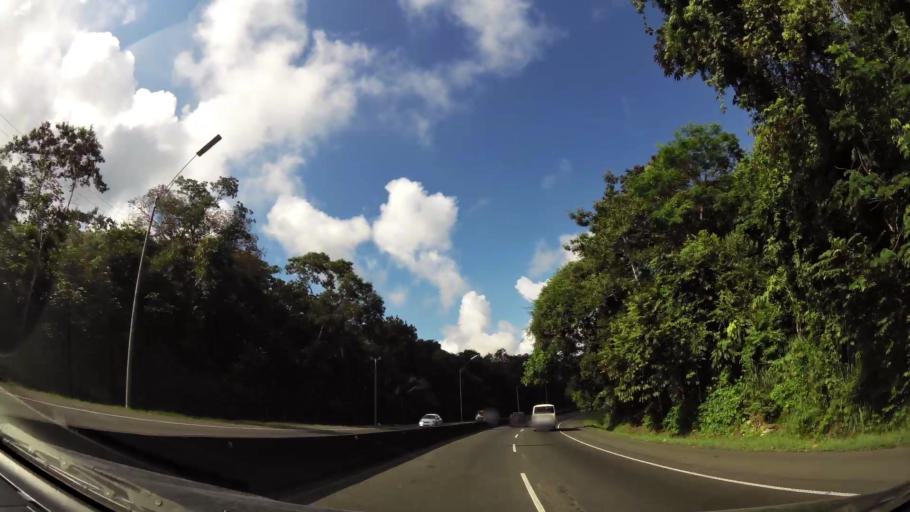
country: PA
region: Panama
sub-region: Distrito Arraijan
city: Arraijan
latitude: 8.9546
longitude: -79.6232
